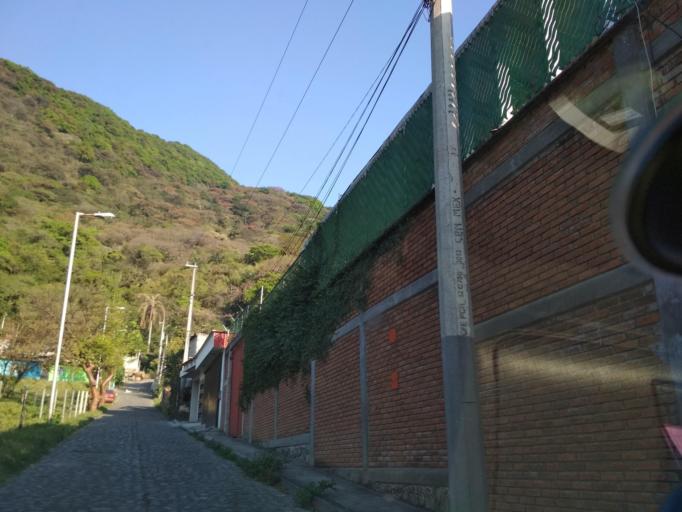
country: MX
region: Veracruz
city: Orizaba
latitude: 18.8603
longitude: -97.0817
